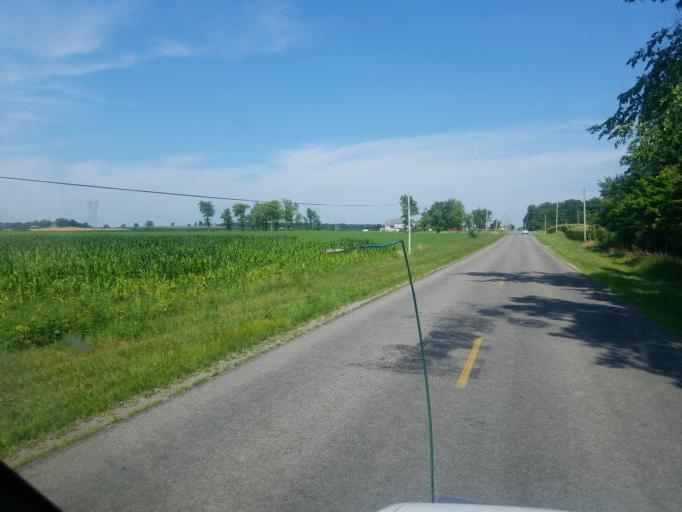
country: US
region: Ohio
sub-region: Shelby County
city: Jackson Center
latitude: 40.4976
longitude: -84.0910
